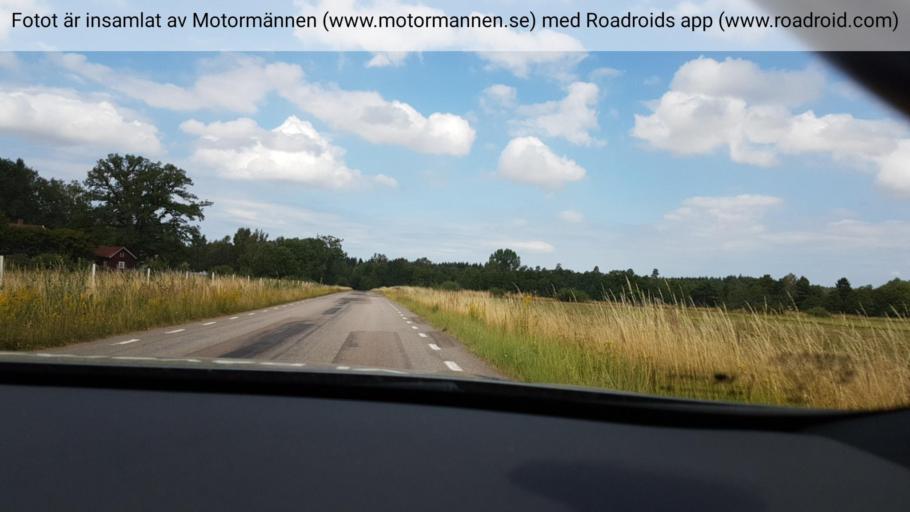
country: SE
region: Vaestra Goetaland
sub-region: Lidkopings Kommun
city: Vinninga
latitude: 58.4254
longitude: 13.3502
